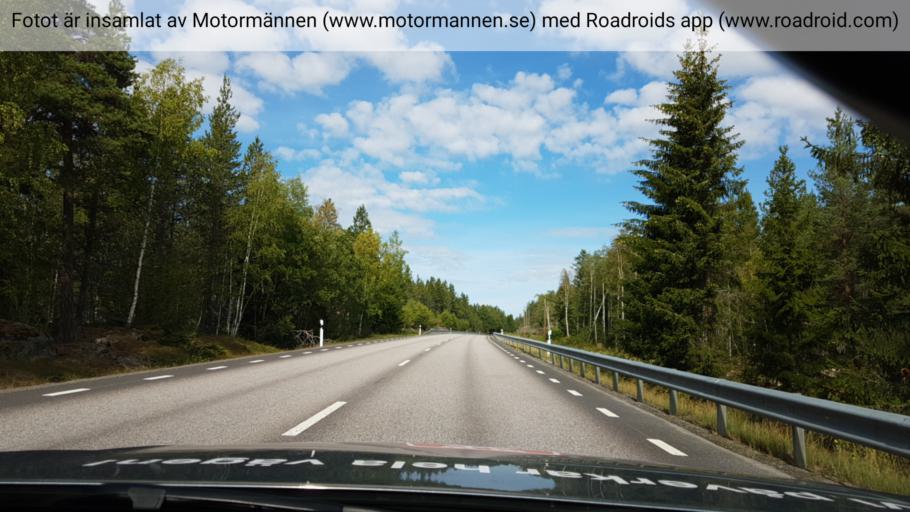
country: SE
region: Uppsala
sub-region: Osthammars Kommun
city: Bjorklinge
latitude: 59.9810
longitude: 17.3373
